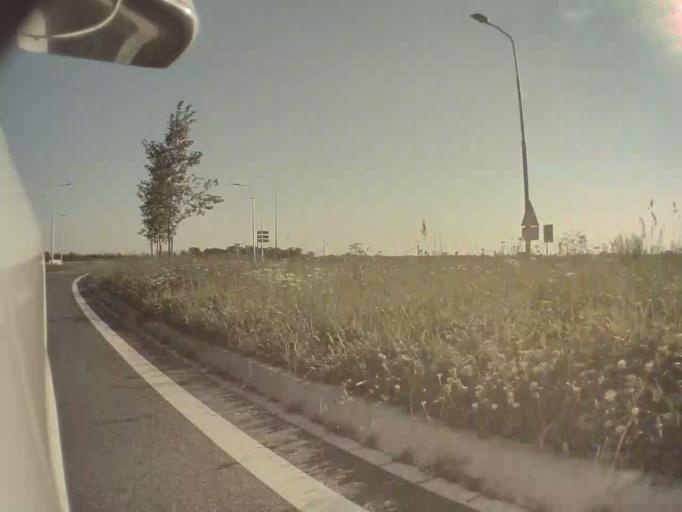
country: NL
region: South Holland
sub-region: Gemeente Pijnacker-Nootdorp
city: Pijnacker
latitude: 52.0056
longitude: 4.4185
